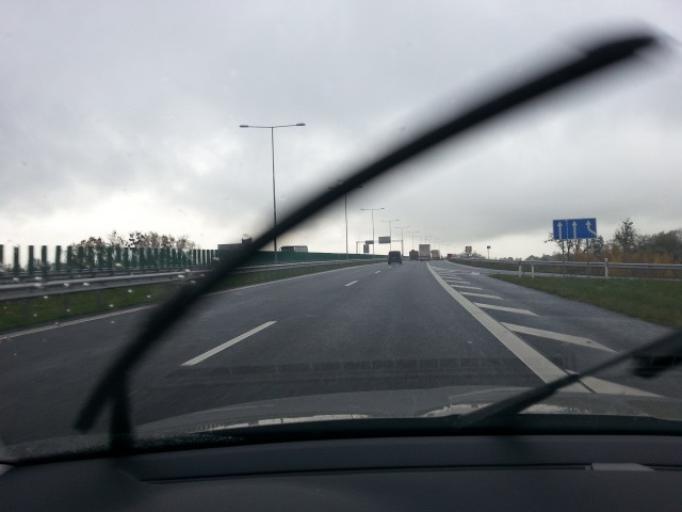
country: LT
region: Kauno apskritis
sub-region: Kauno rajonas
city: Mastaiciai
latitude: 54.7803
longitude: 23.7791
